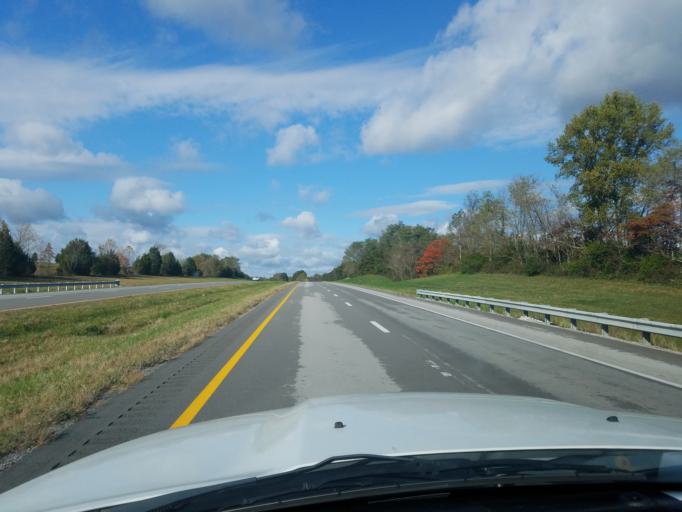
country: US
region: Kentucky
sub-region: Pulaski County
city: Somerset
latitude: 37.0981
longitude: -84.7599
